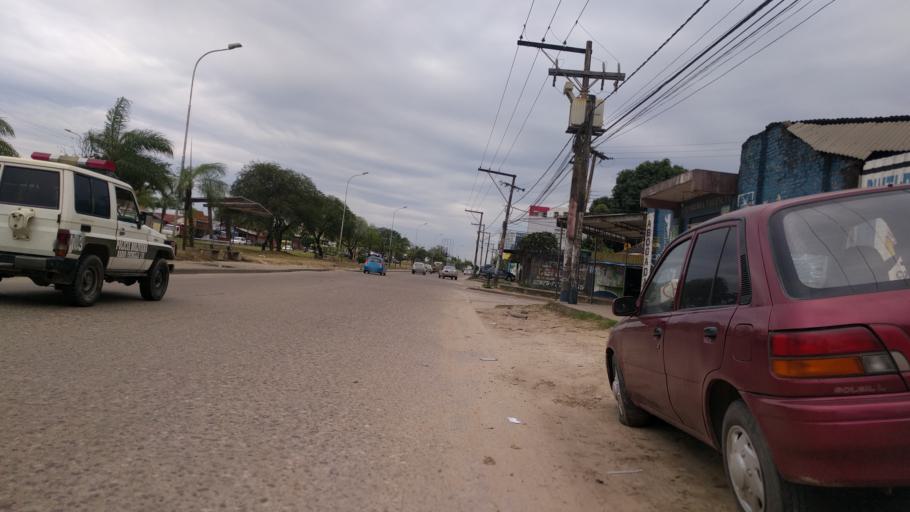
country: BO
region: Santa Cruz
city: Santa Cruz de la Sierra
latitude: -17.8190
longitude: -63.1981
